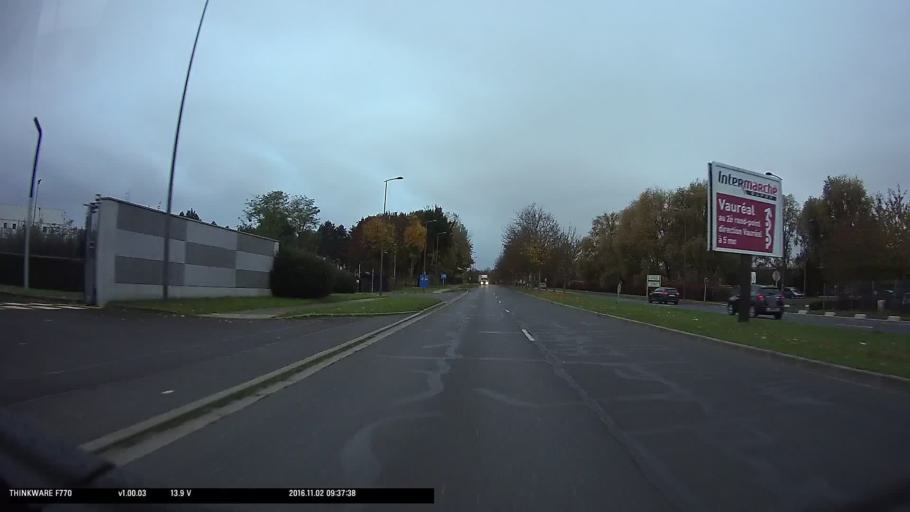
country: FR
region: Ile-de-France
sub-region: Departement du Val-d'Oise
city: Vaureal
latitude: 49.0566
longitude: 2.0284
